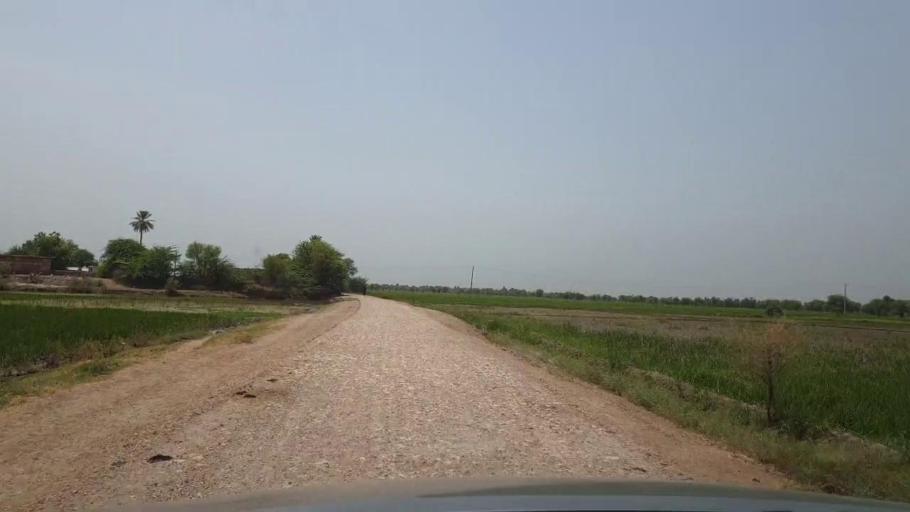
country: PK
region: Sindh
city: Madeji
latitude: 27.7757
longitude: 68.4060
